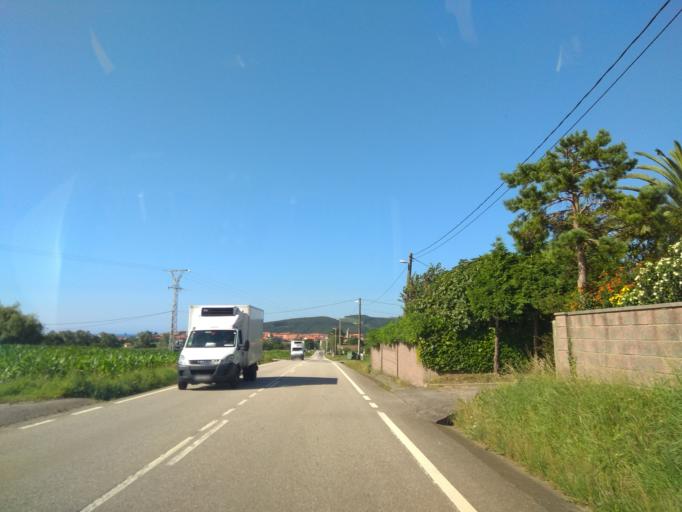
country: ES
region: Cantabria
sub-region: Provincia de Cantabria
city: Bareyo
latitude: 43.4597
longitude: -3.6745
